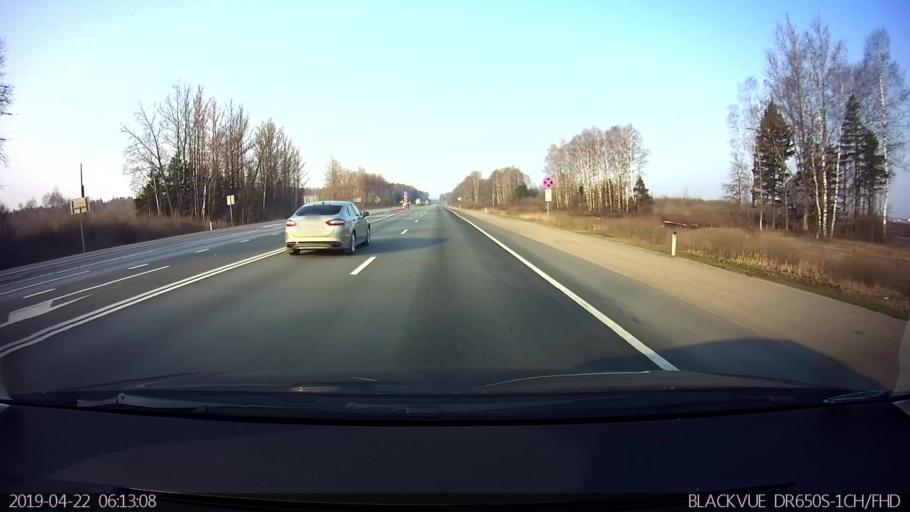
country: RU
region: Moskovskaya
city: Mozhaysk
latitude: 55.4741
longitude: 36.1096
